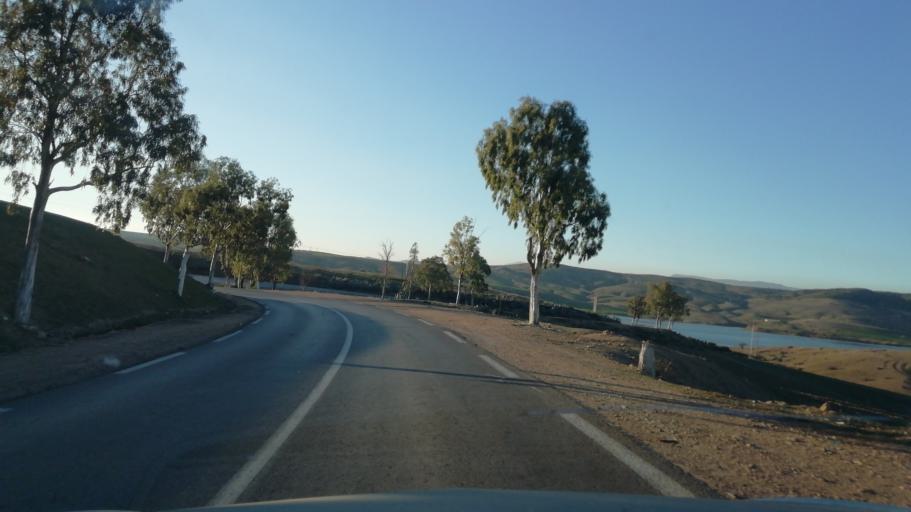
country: DZ
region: Tlemcen
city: Nedroma
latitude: 34.8287
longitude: -1.6455
